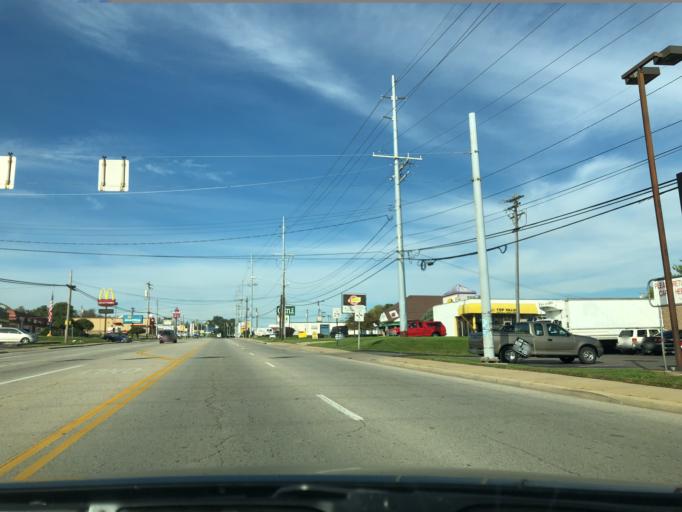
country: US
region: Ohio
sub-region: Hamilton County
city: Glendale
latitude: 39.2853
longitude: -84.4432
